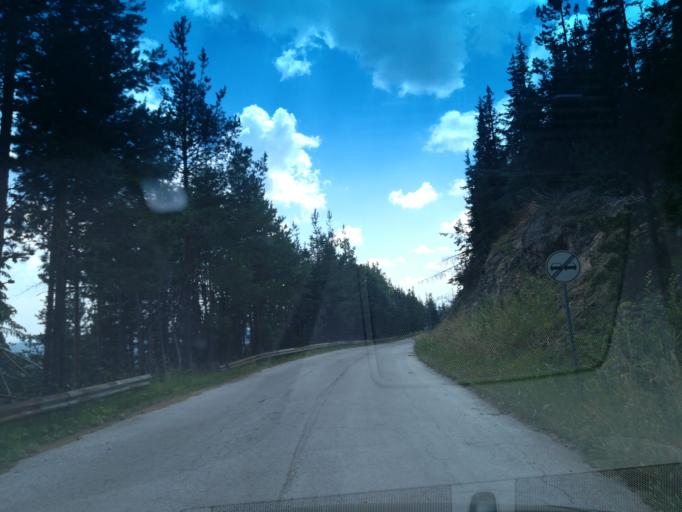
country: BG
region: Smolyan
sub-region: Obshtina Chepelare
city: Chepelare
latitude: 41.6857
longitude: 24.7528
